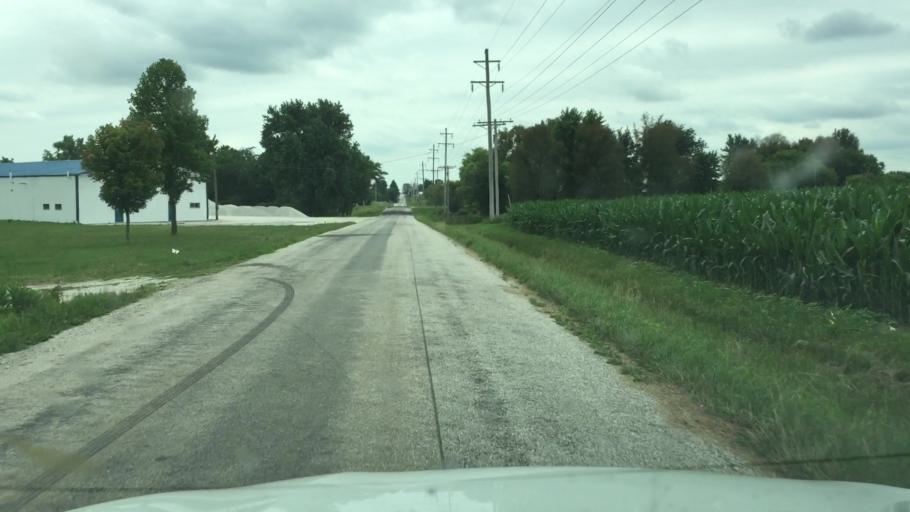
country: US
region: Illinois
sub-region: Hancock County
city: Carthage
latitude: 40.3326
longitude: -91.0825
